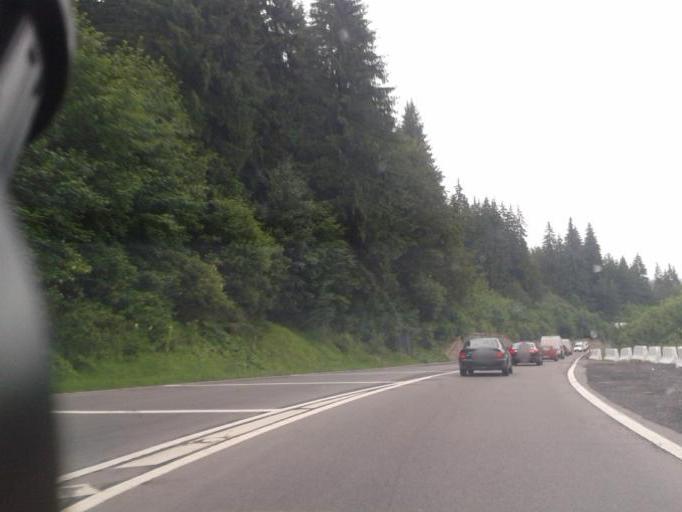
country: RO
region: Brasov
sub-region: Oras Predeal
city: Predeal
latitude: 45.5191
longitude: 25.5730
